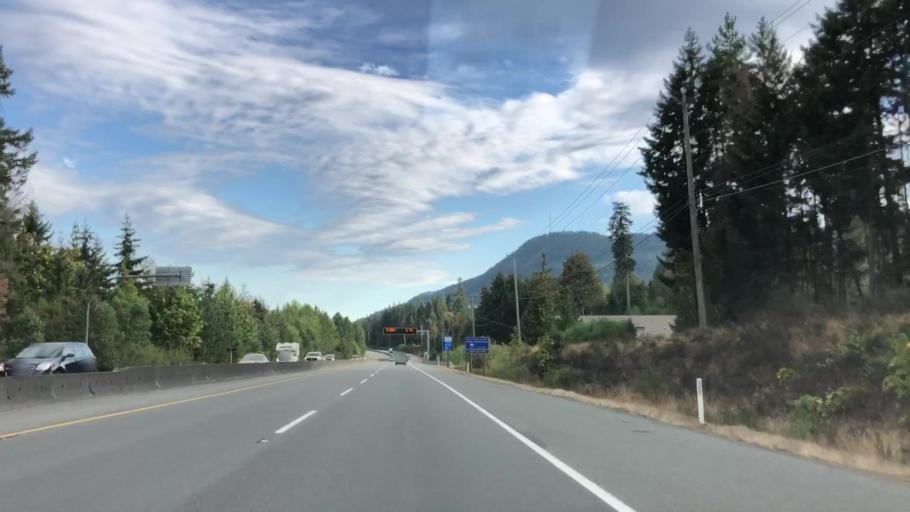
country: CA
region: British Columbia
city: North Saanich
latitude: 48.6265
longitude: -123.5479
